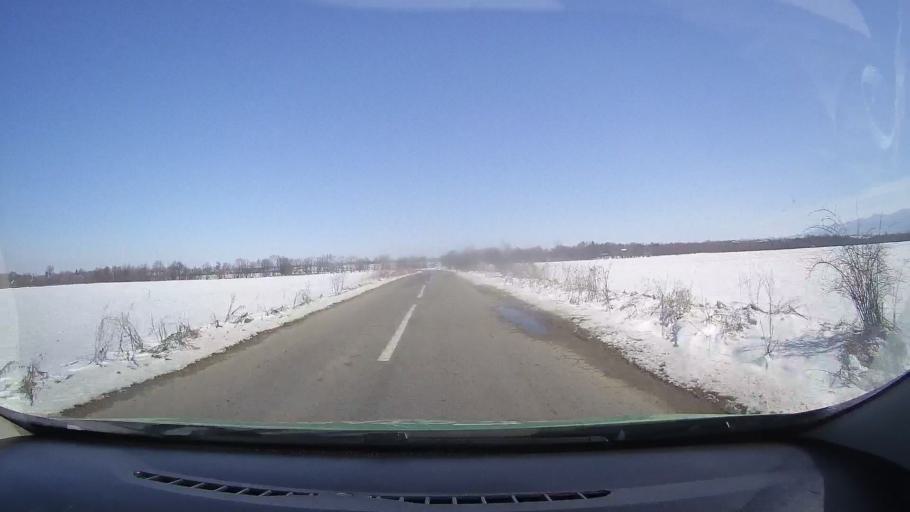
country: RO
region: Brasov
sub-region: Comuna Harseni
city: Harseni
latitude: 45.7323
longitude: 24.9970
